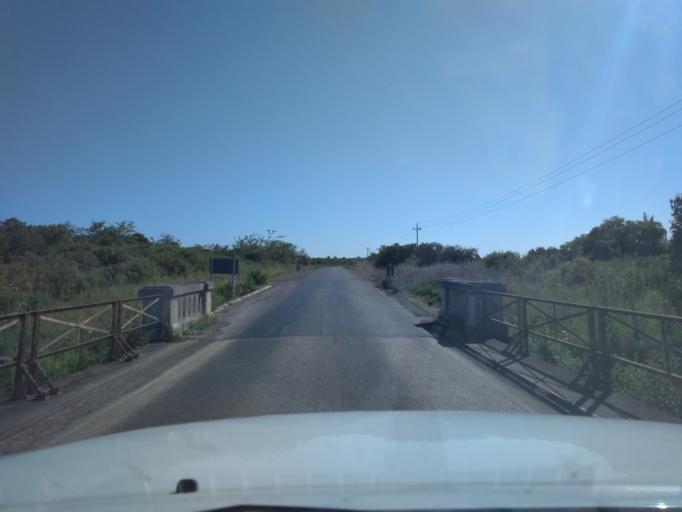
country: UY
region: Canelones
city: San Ramon
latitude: -34.2705
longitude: -55.9420
